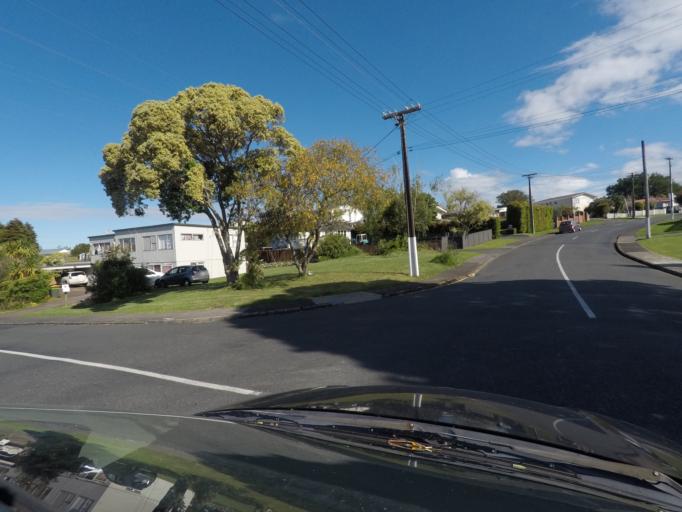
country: NZ
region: Auckland
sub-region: Auckland
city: Rosebank
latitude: -36.8692
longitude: 174.6494
